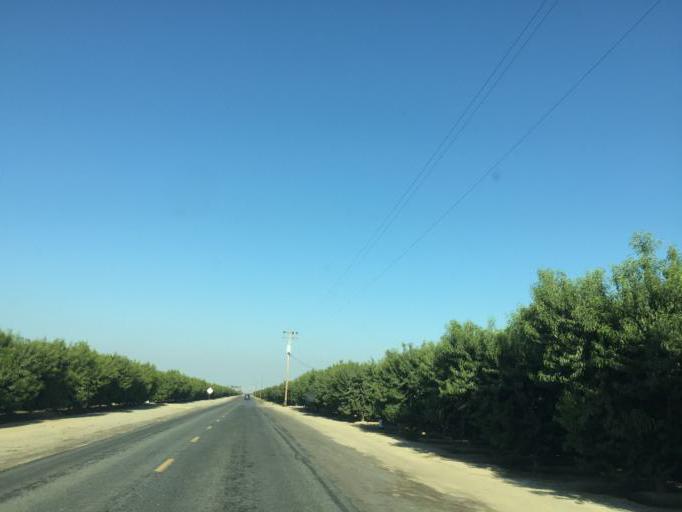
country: US
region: California
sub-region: Tulare County
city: London
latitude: 36.4589
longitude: -119.4734
